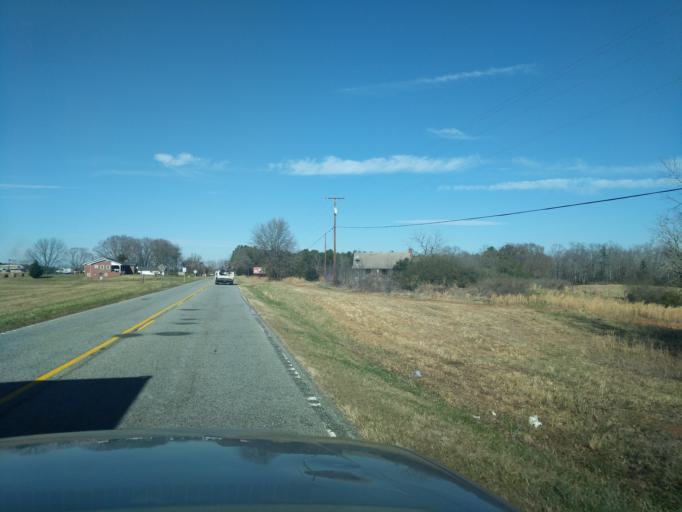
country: US
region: South Carolina
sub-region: Spartanburg County
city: Mayo
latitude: 35.1694
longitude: -81.8435
